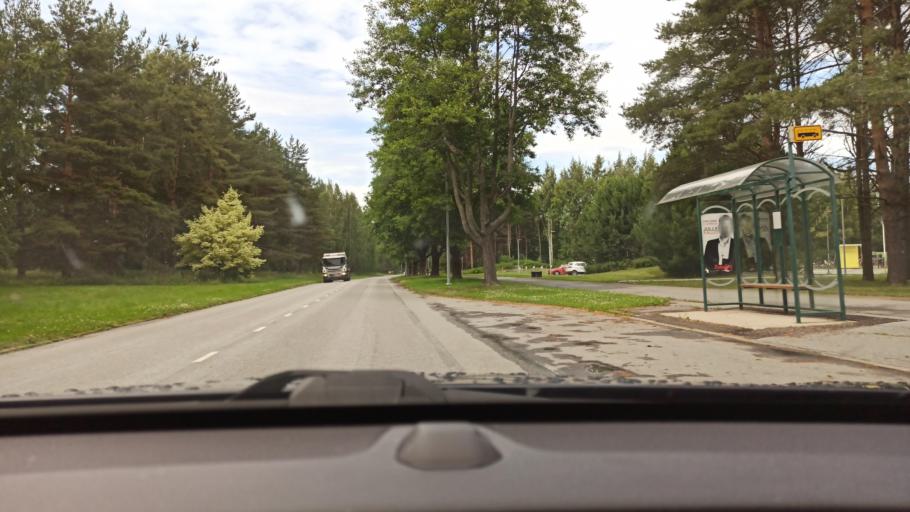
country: FI
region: Satakunta
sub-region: Pori
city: Pori
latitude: 61.4987
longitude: 21.7861
